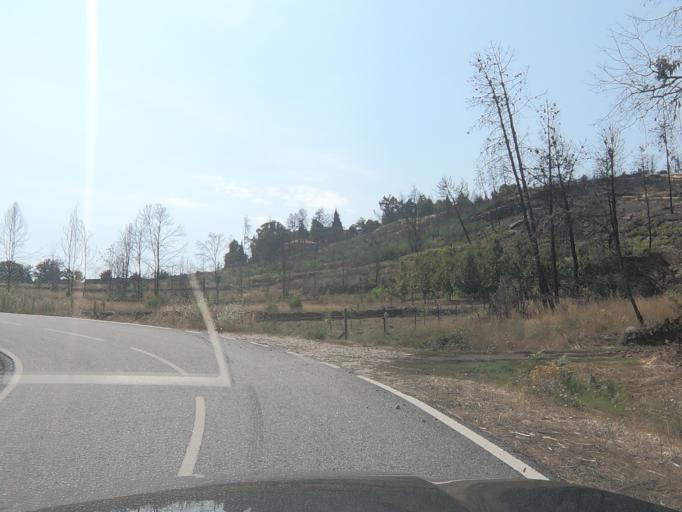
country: PT
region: Vila Real
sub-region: Sabrosa
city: Sabrosa
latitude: 41.3389
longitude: -7.5952
